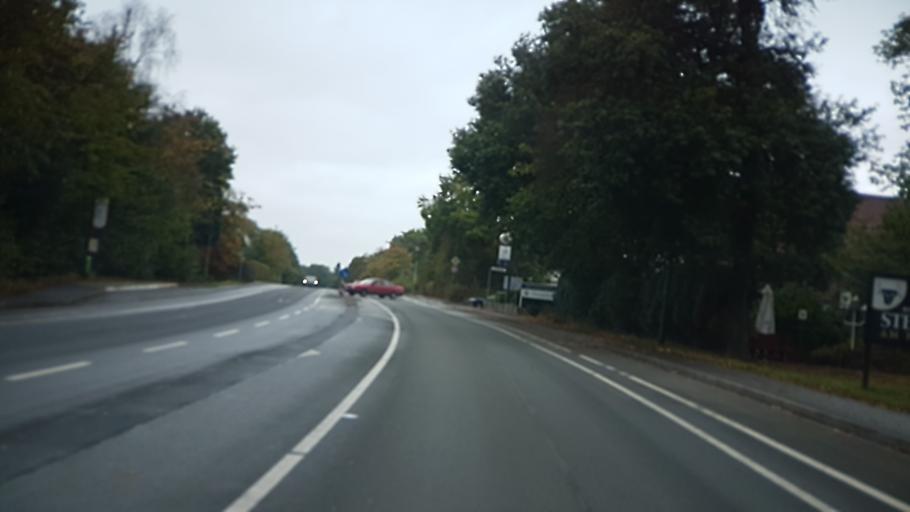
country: DE
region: North Rhine-Westphalia
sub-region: Regierungsbezirk Arnsberg
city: Luedenscheid
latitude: 51.1978
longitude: 7.6661
